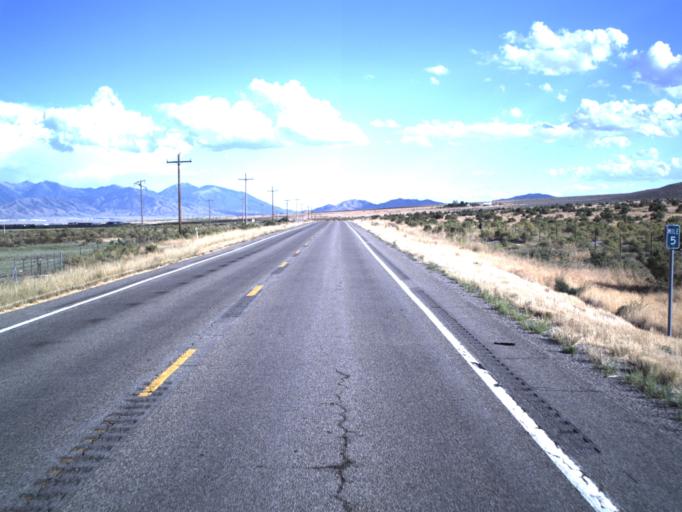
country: US
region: Utah
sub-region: Tooele County
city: Grantsville
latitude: 40.6494
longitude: -112.5309
